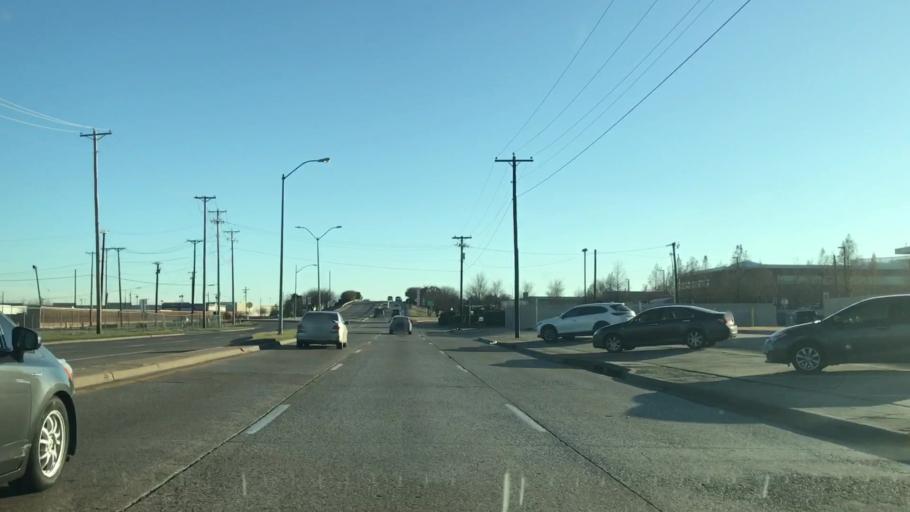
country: US
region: Texas
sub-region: Dallas County
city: Mesquite
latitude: 32.8006
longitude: -96.6683
